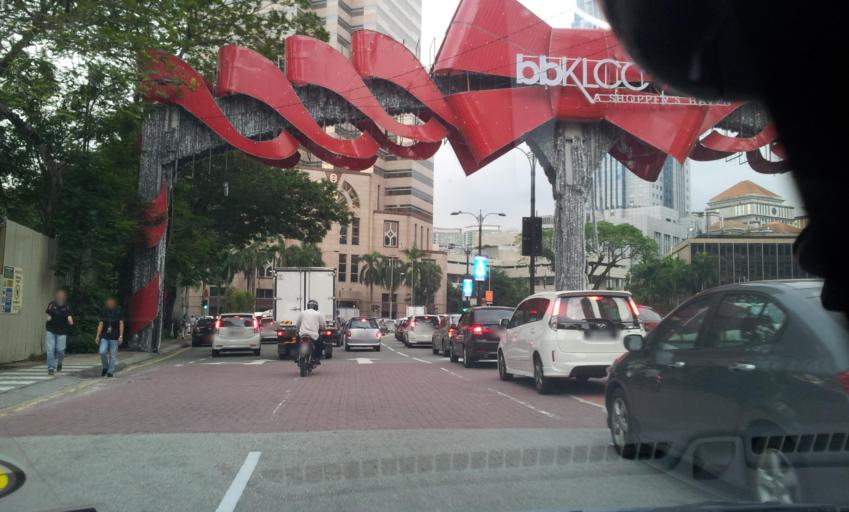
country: MY
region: Kuala Lumpur
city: Kuala Lumpur
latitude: 3.1584
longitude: 101.7105
